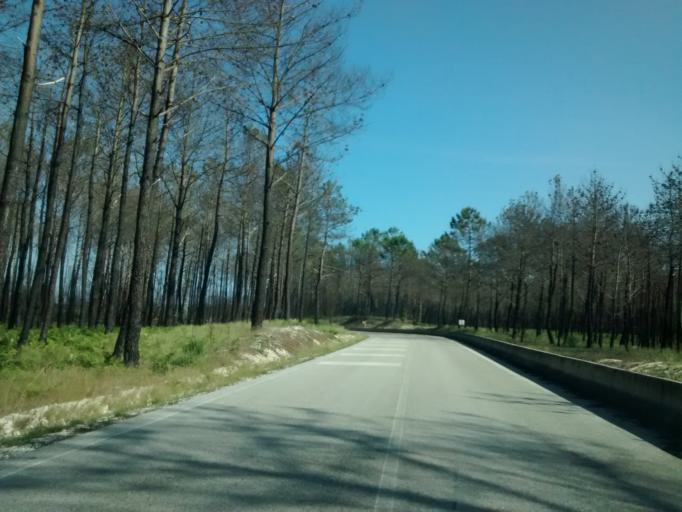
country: PT
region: Coimbra
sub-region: Figueira da Foz
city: Lavos
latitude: 40.0000
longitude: -8.8633
